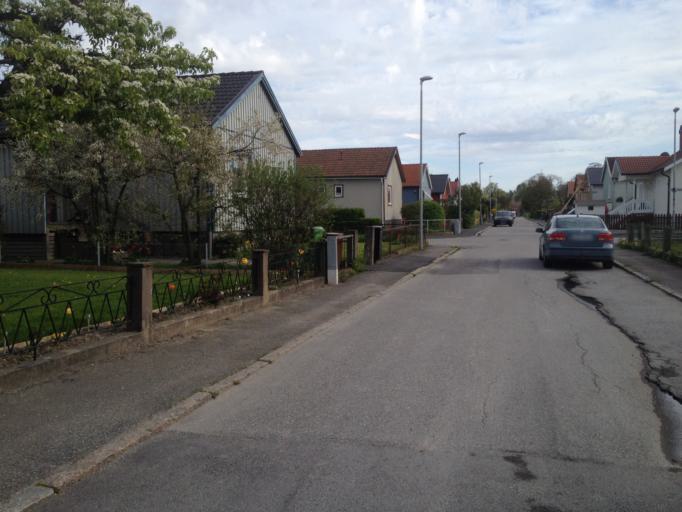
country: SE
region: OEstergoetland
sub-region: Norrkopings Kommun
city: Norrkoping
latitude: 58.6035
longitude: 16.1734
